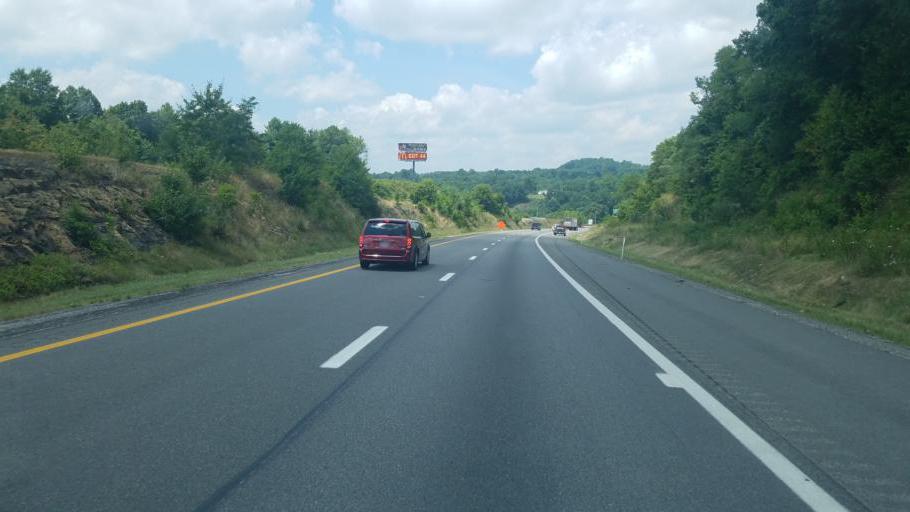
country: US
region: West Virginia
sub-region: Raleigh County
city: MacArthur
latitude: 37.7372
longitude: -81.2066
